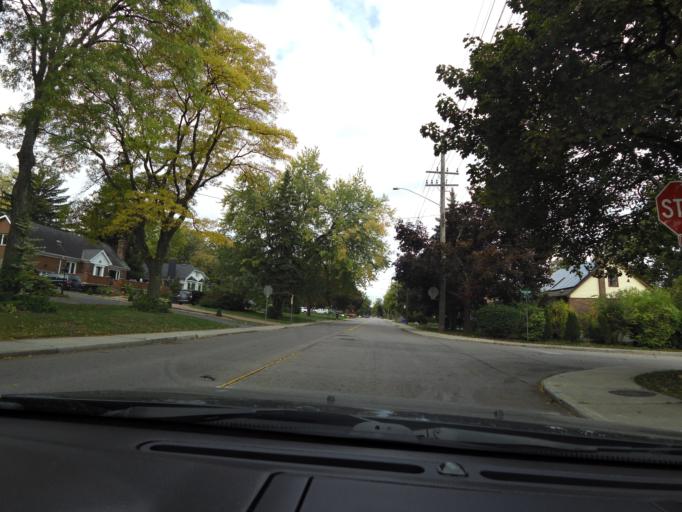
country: CA
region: Ontario
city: Hamilton
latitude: 43.2352
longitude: -79.9070
